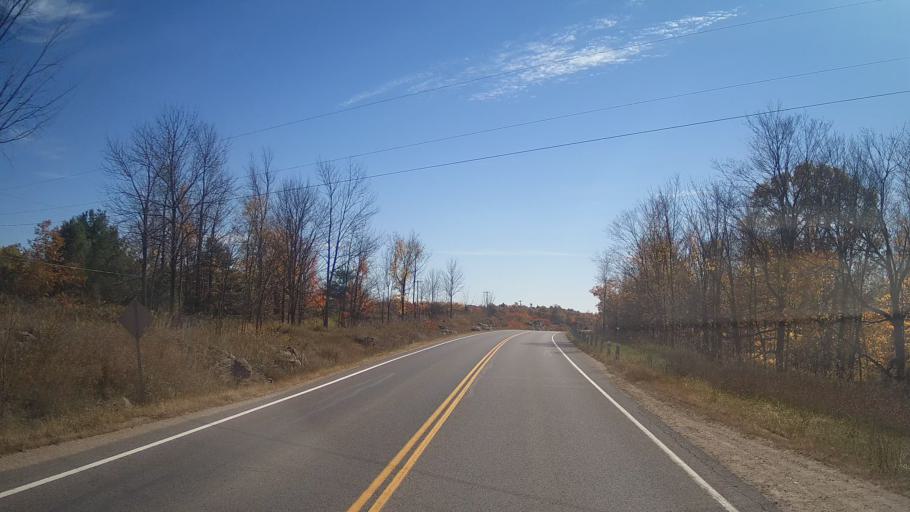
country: CA
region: Ontario
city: Perth
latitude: 44.6838
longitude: -76.6729
